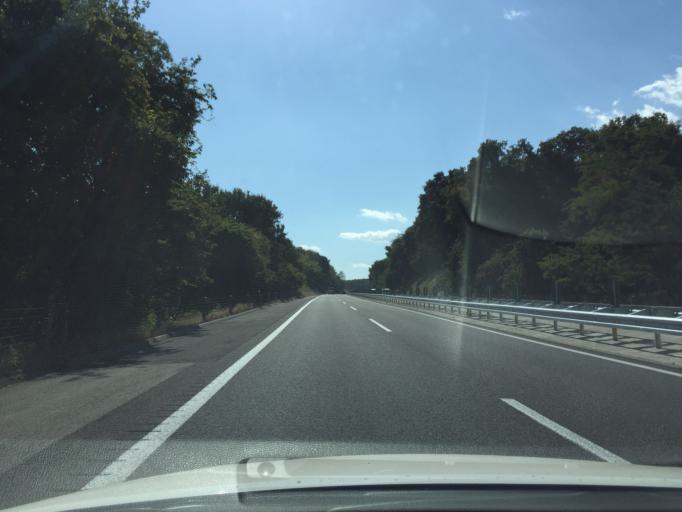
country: JP
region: Fukushima
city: Sukagawa
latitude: 37.2366
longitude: 140.3275
